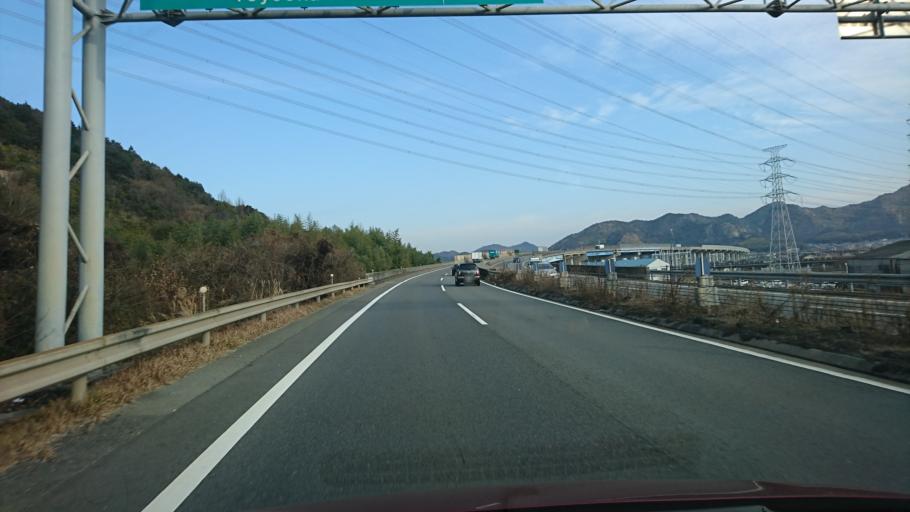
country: JP
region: Hyogo
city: Shirahamacho-usazakiminami
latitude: 34.8070
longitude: 134.7431
